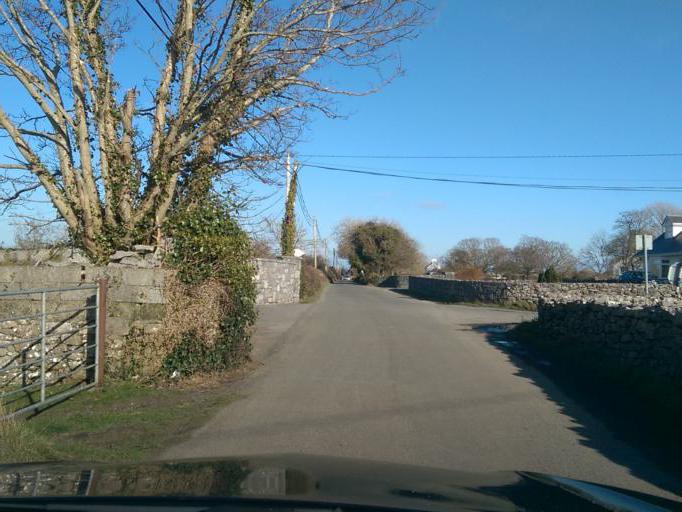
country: IE
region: Connaught
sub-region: County Galway
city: Oranmore
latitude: 53.2330
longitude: -8.9576
